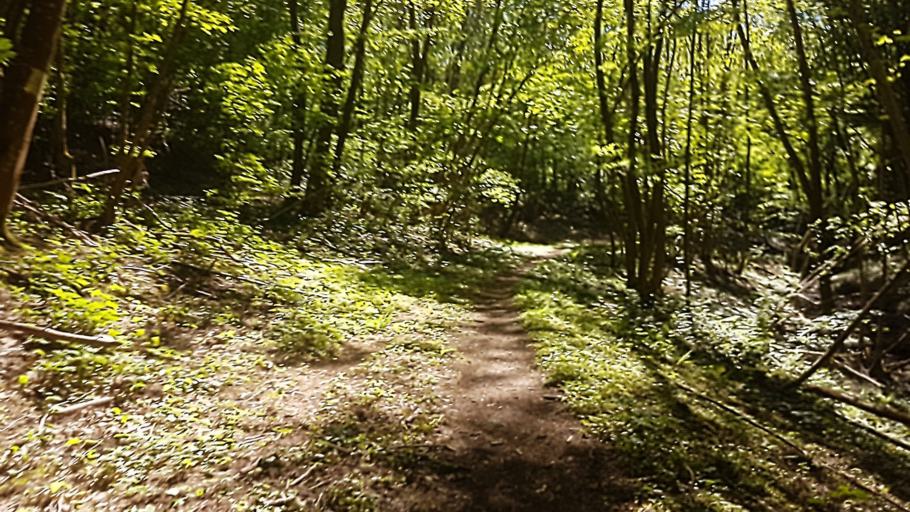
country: BE
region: Wallonia
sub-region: Province de Namur
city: Couvin
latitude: 50.0589
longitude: 4.5763
